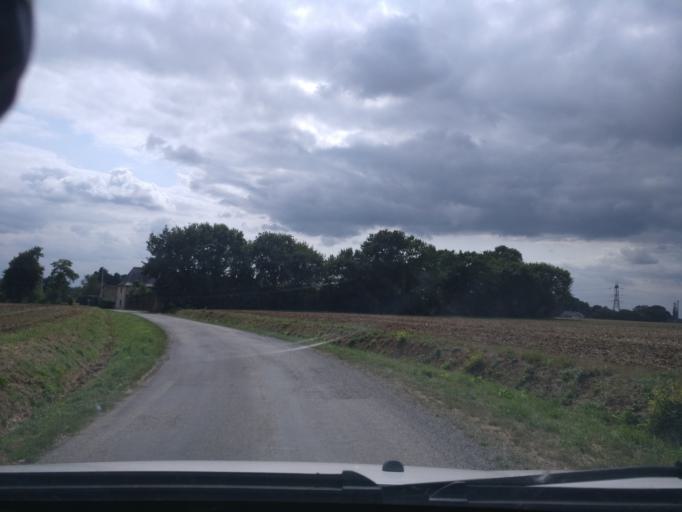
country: FR
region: Brittany
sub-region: Departement d'Ille-et-Vilaine
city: Noyal-sur-Vilaine
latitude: 48.0824
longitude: -1.5322
